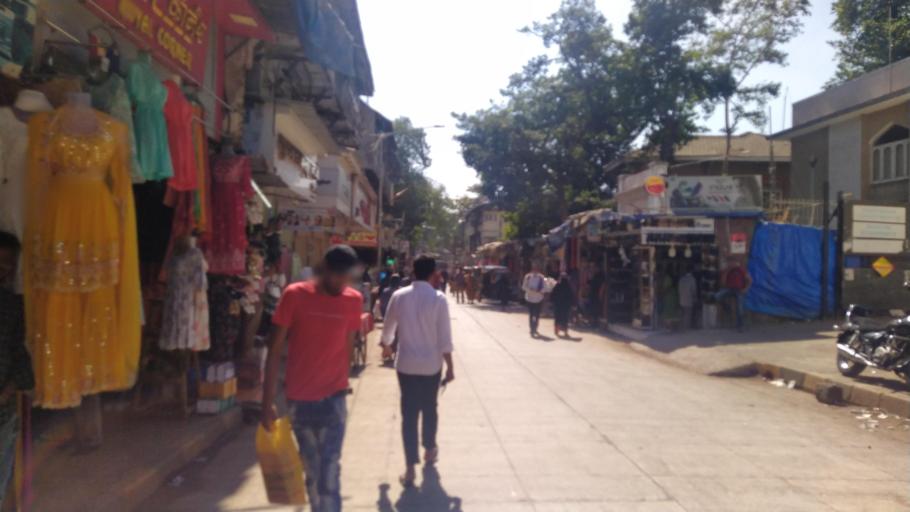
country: IN
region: Maharashtra
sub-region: Mumbai Suburban
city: Mumbai
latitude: 19.0663
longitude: 72.8774
